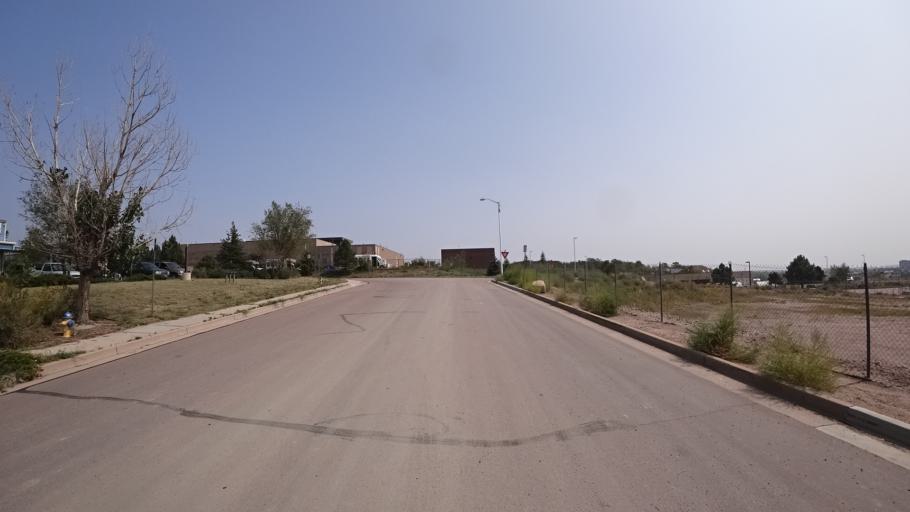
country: US
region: Colorado
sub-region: El Paso County
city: Colorado Springs
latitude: 38.8166
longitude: -104.8067
